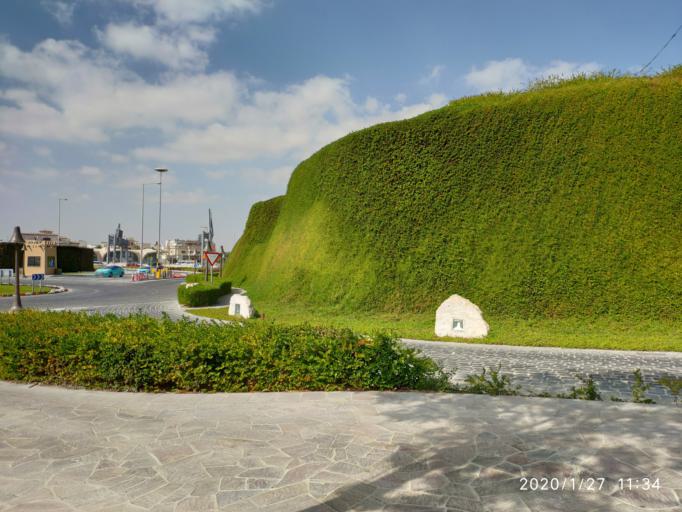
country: QA
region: Baladiyat ad Dawhah
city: Doha
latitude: 25.3628
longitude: 51.5231
